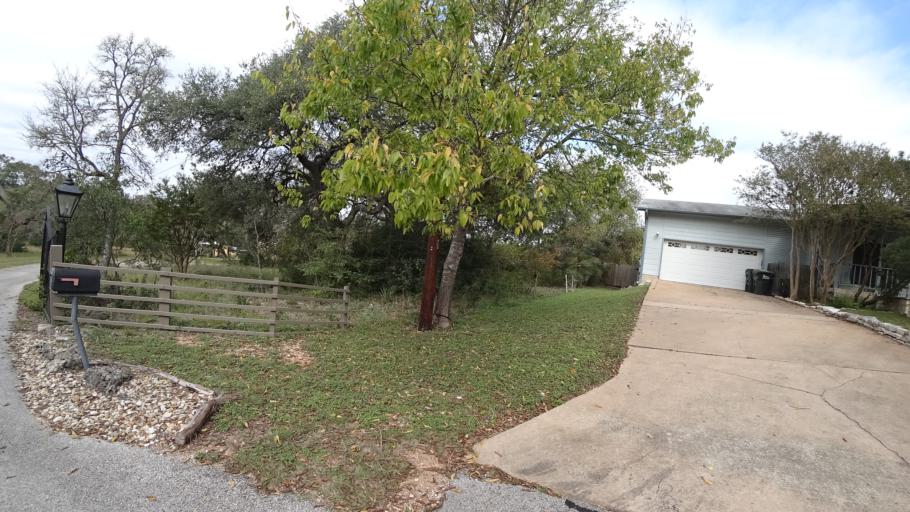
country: US
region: Texas
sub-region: Travis County
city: Shady Hollow
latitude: 30.1332
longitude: -97.8929
